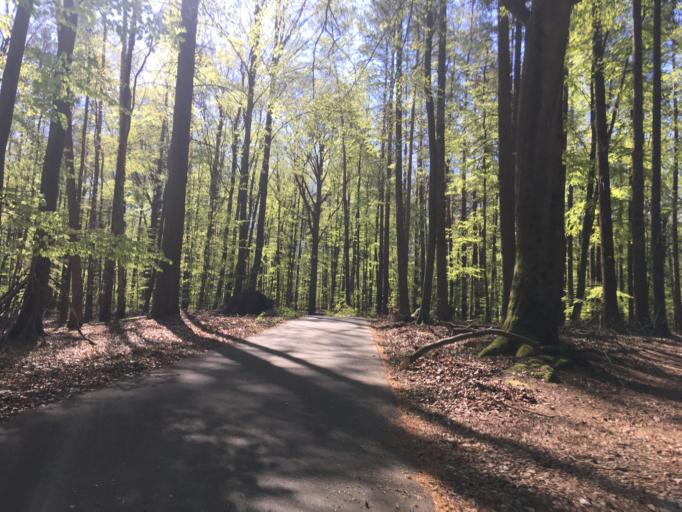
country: DE
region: Brandenburg
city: Wandlitz
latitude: 52.7407
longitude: 13.4936
